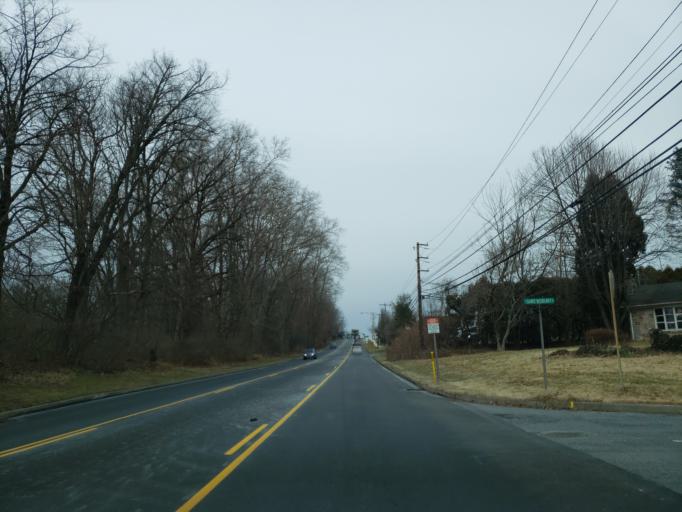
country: US
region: Pennsylvania
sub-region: Lehigh County
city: Dorneyville
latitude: 40.5941
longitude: -75.5264
